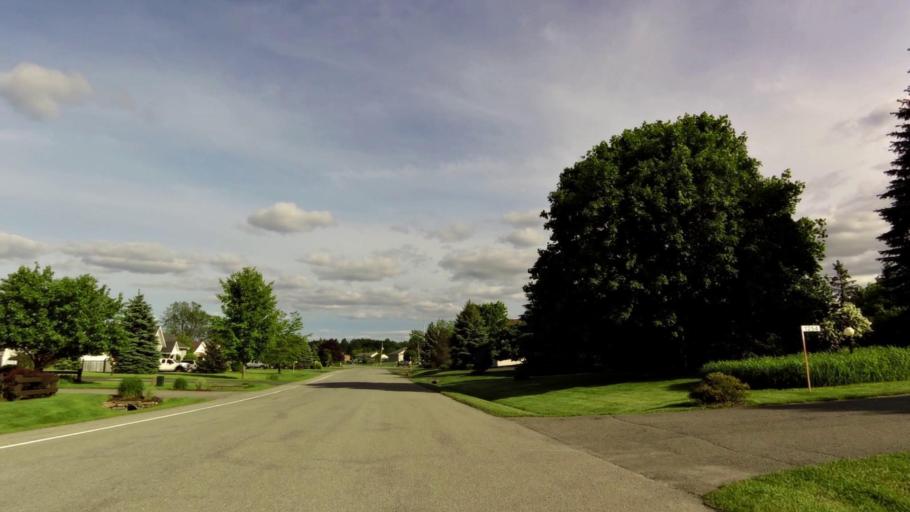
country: CA
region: Ontario
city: Ottawa
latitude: 45.2670
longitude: -75.5679
